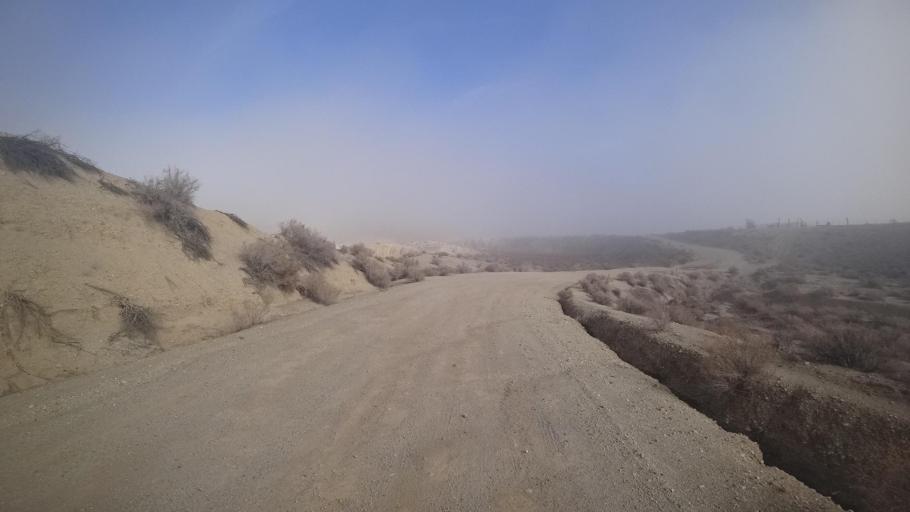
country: US
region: California
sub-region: Kern County
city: Maricopa
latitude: 35.0216
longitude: -119.4479
